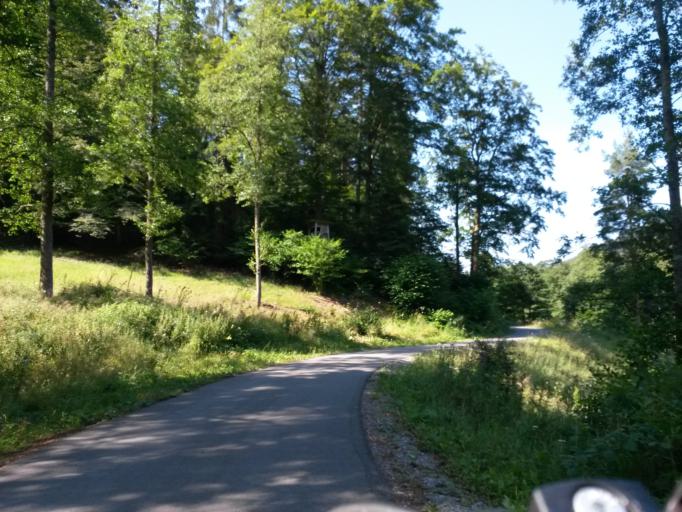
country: DE
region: Baden-Wuerttemberg
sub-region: Karlsruhe Region
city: Enzklosterle
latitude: 48.6845
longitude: 8.4902
